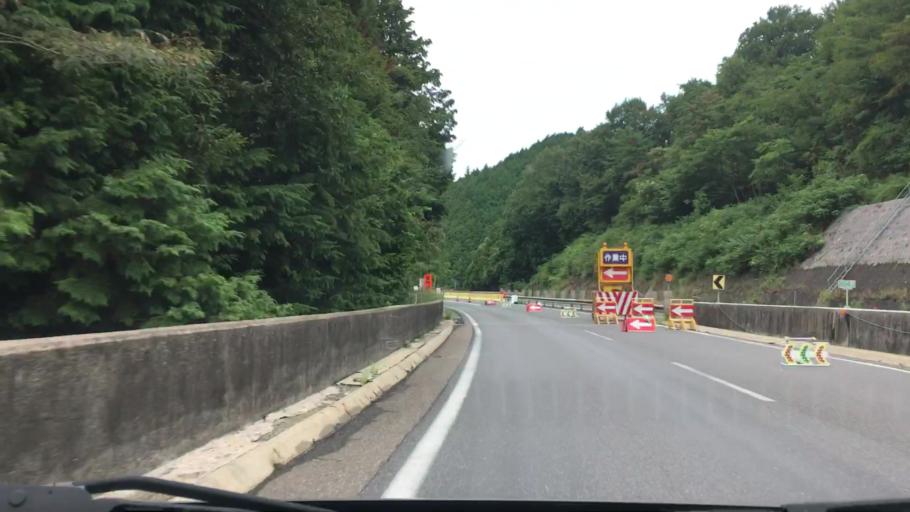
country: JP
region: Okayama
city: Niimi
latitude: 35.0185
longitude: 133.5833
